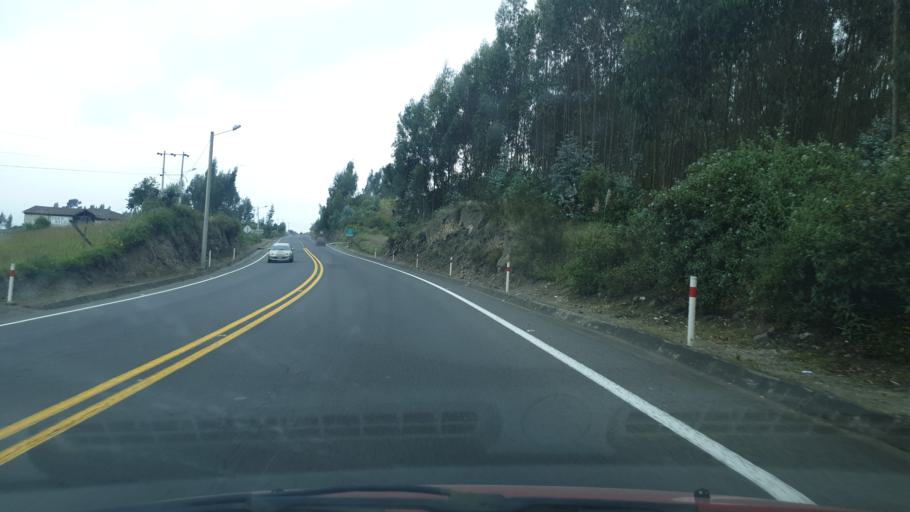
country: EC
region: Tungurahua
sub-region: Canton Quero
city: Quero
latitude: -1.3792
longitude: -78.6497
